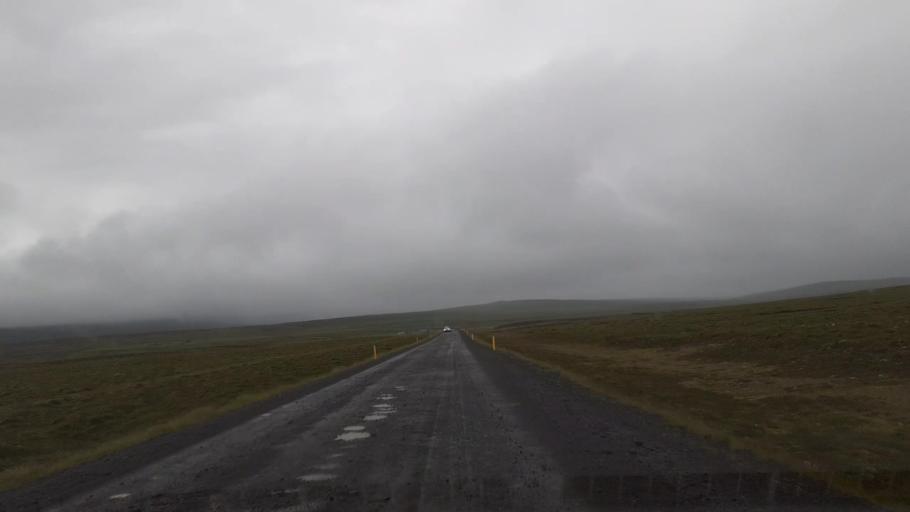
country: IS
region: East
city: Egilsstadir
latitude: 66.0501
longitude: -15.0926
